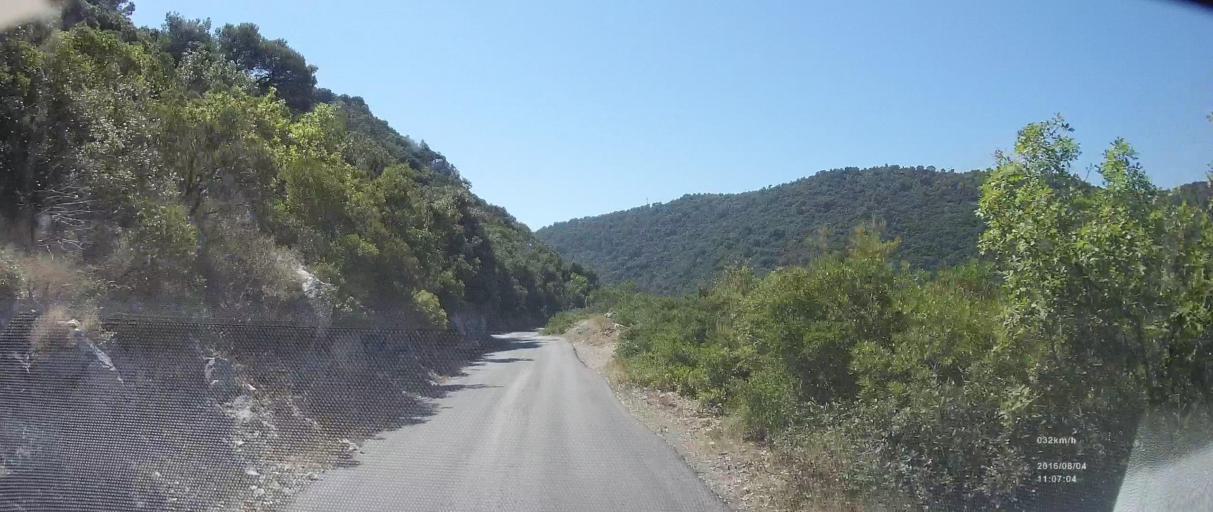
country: HR
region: Dubrovacko-Neretvanska
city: Blato
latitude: 42.7697
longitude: 17.4665
